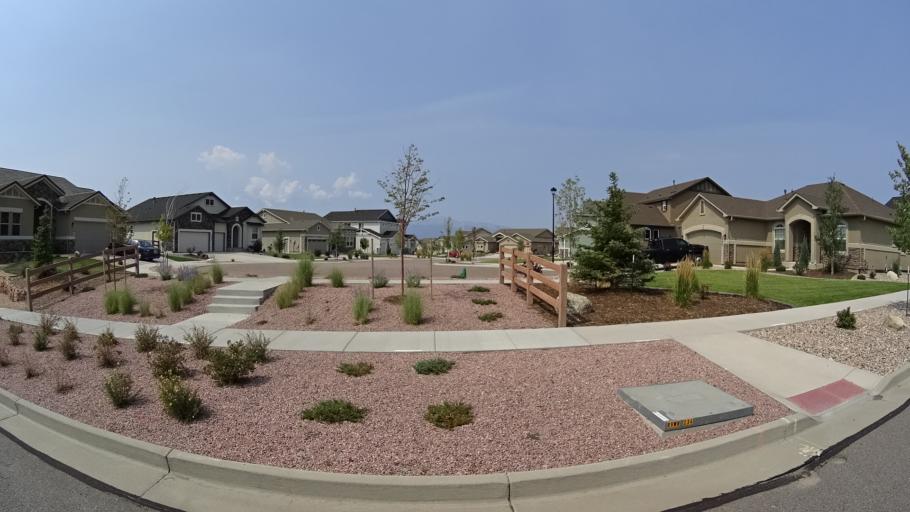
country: US
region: Colorado
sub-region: El Paso County
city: Black Forest
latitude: 38.9693
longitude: -104.7233
